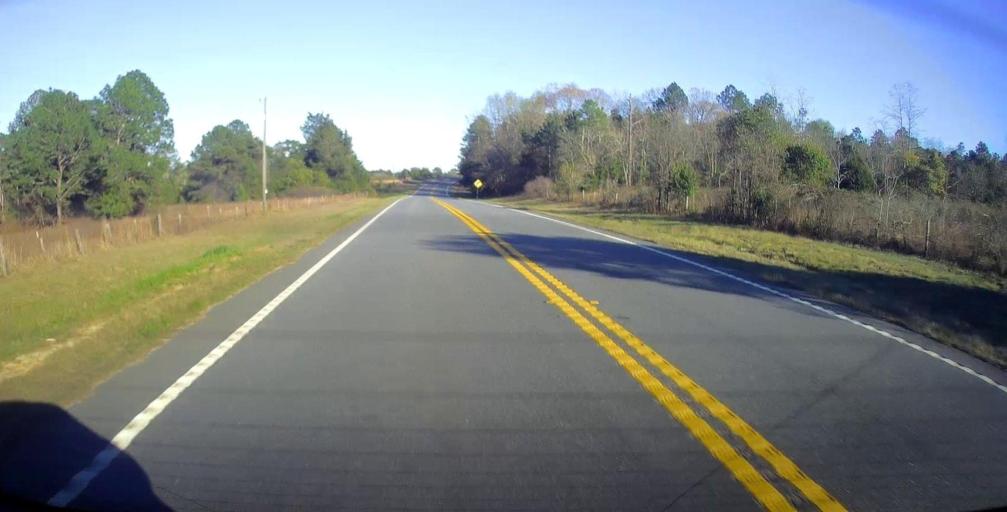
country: US
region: Georgia
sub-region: Taylor County
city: Butler
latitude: 32.4733
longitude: -84.3696
